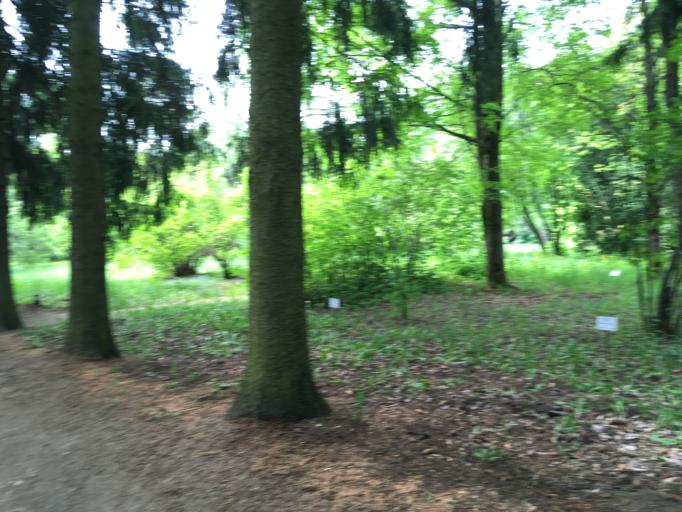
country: BY
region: Minsk
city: Minsk
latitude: 53.9151
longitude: 27.6136
